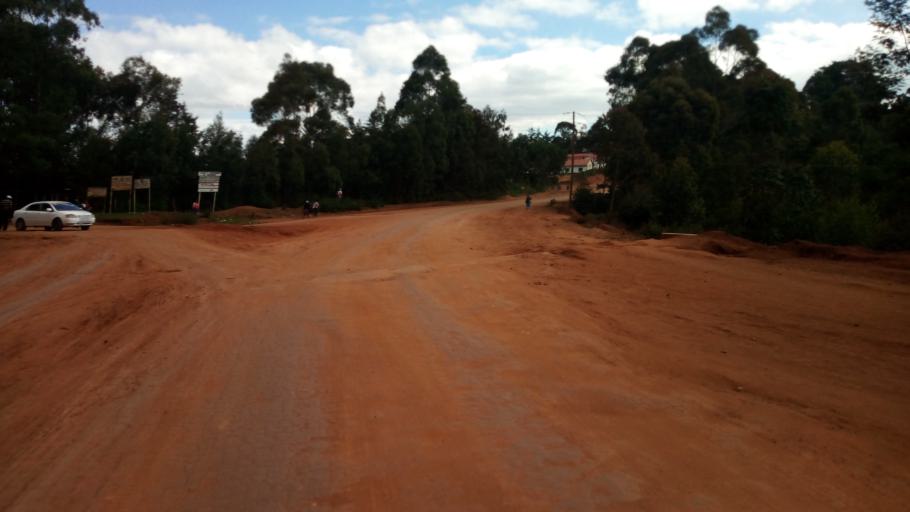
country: KE
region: Makueni
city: Wote
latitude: -1.6571
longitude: 37.4532
